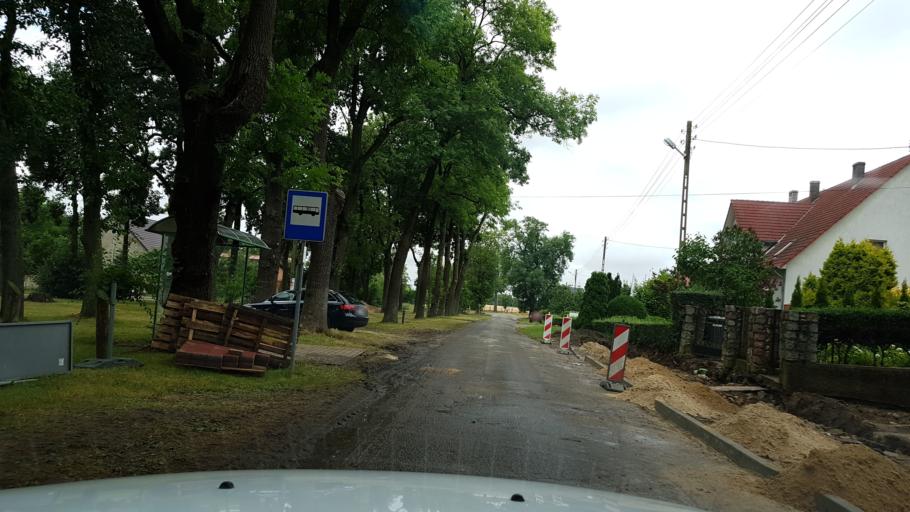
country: PL
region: West Pomeranian Voivodeship
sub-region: Powiat pyrzycki
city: Przelewice
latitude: 53.1080
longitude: 15.1261
